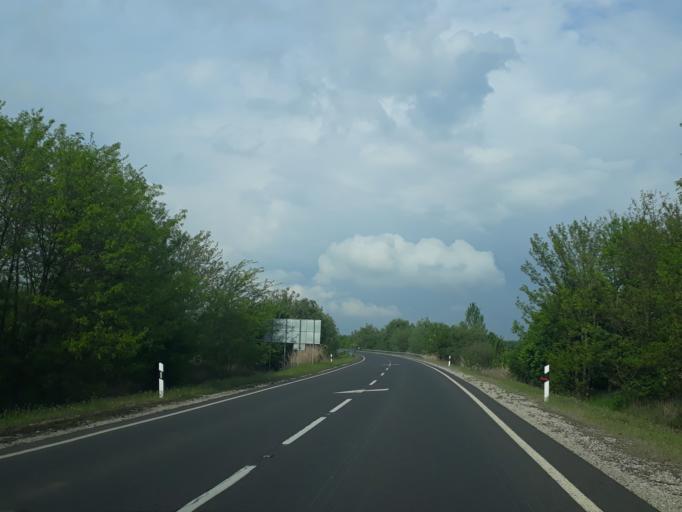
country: HU
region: Szabolcs-Szatmar-Bereg
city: Nyirtass
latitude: 48.0816
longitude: 21.9810
